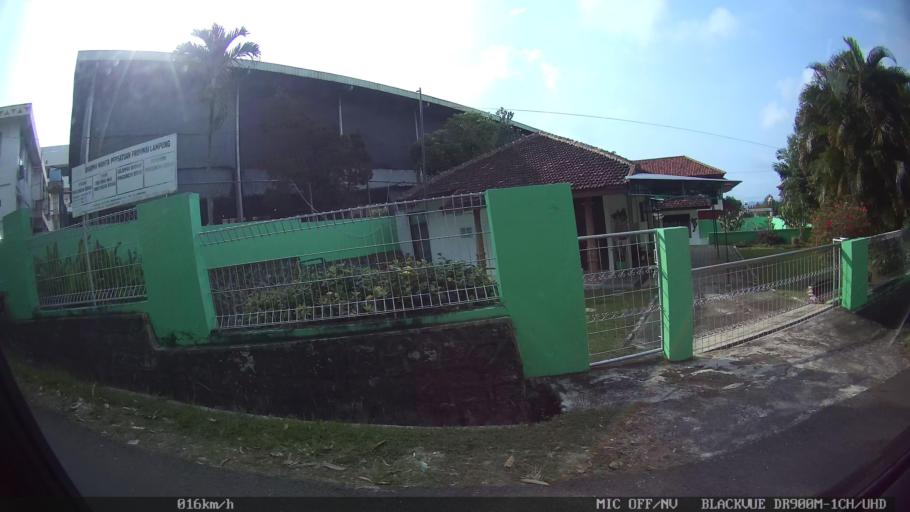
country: ID
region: Lampung
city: Bandarlampung
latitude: -5.4413
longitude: 105.2572
